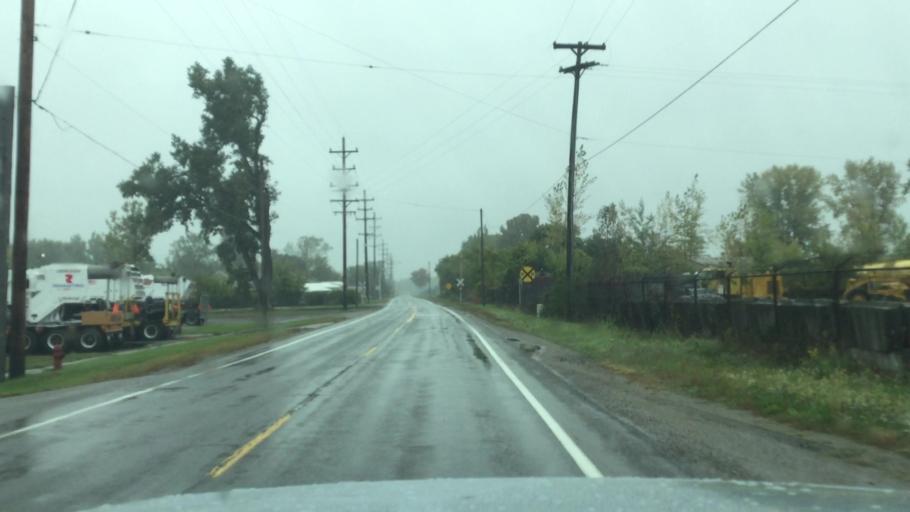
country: US
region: Michigan
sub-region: Saginaw County
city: Carrollton
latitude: 43.4466
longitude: -83.9418
